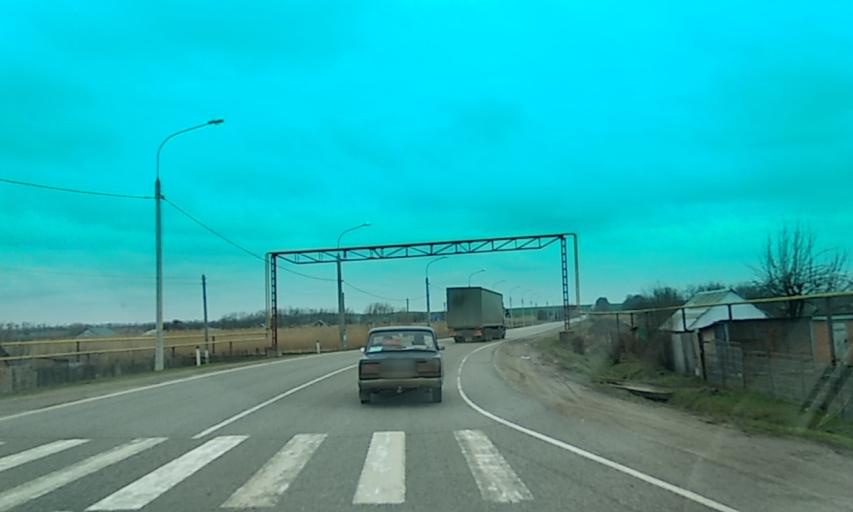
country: RU
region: Krasnodarskiy
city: Vyselki
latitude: 45.4857
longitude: 39.7076
